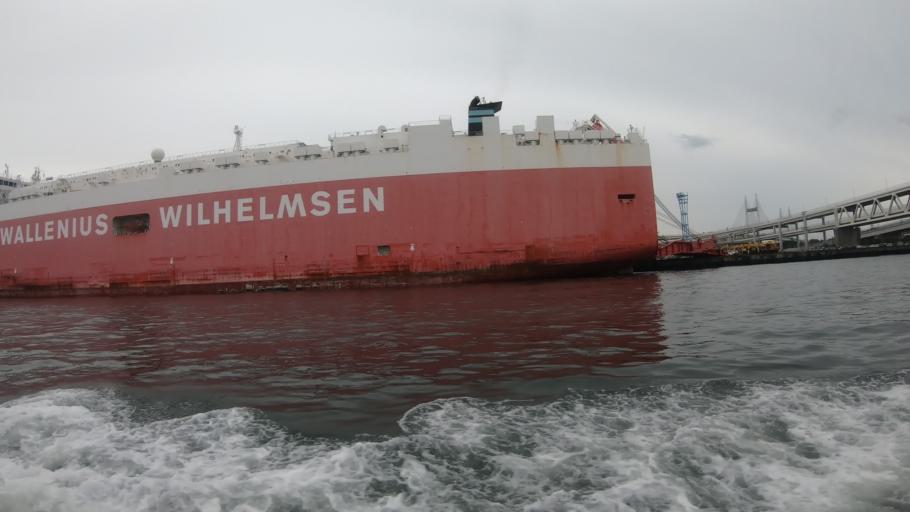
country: JP
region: Kanagawa
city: Yokohama
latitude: 35.4689
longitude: 139.6786
